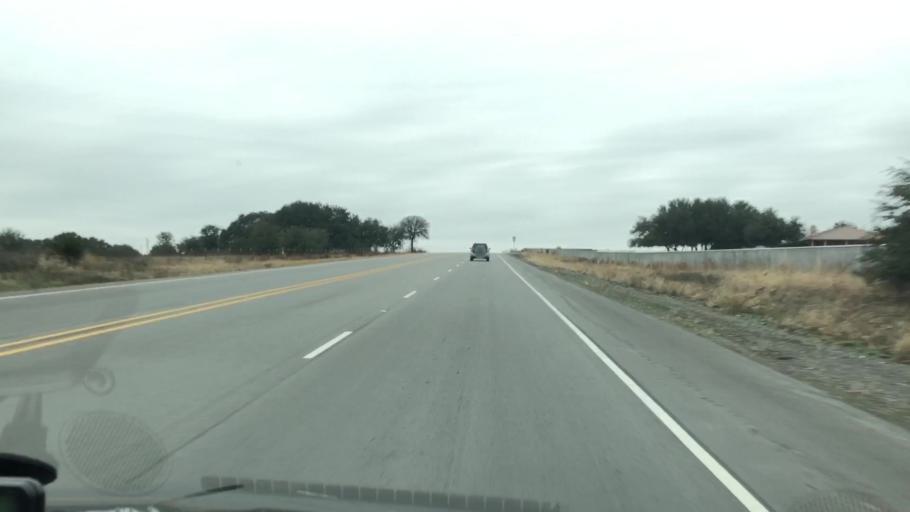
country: US
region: Texas
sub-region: Hamilton County
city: Hico
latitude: 32.0027
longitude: -98.0533
